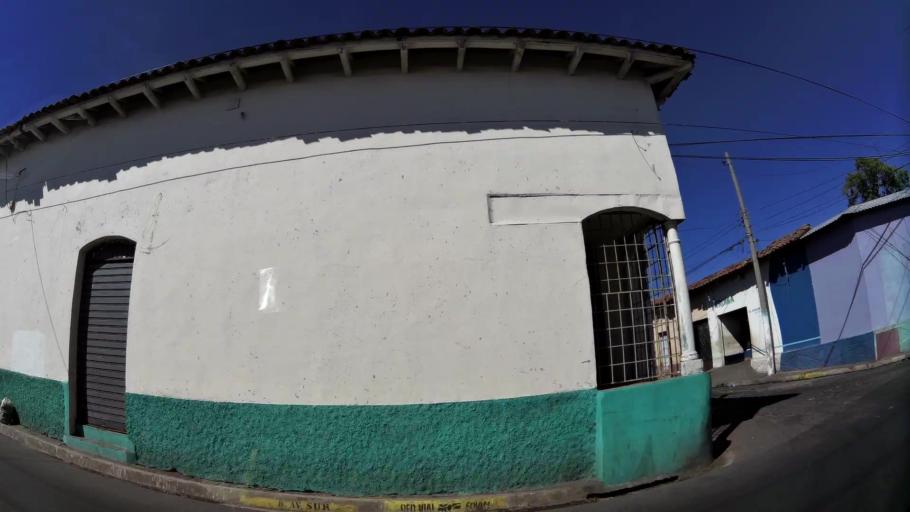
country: SV
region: San Miguel
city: San Miguel
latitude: 13.4802
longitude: -88.1721
